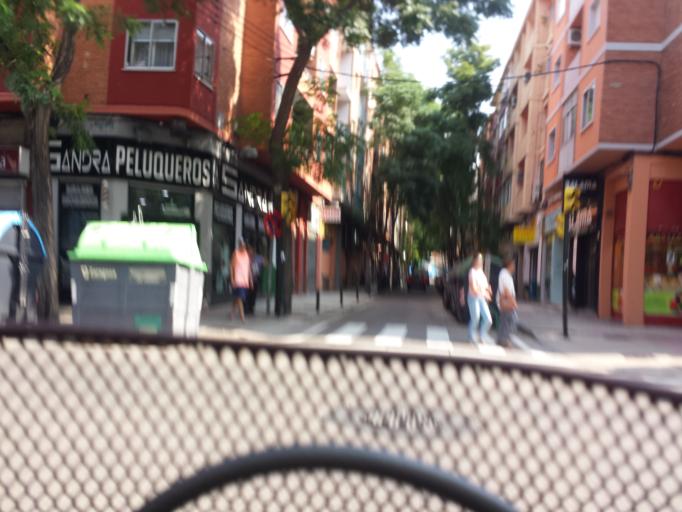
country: ES
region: Aragon
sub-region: Provincia de Zaragoza
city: Delicias
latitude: 41.6504
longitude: -0.9145
